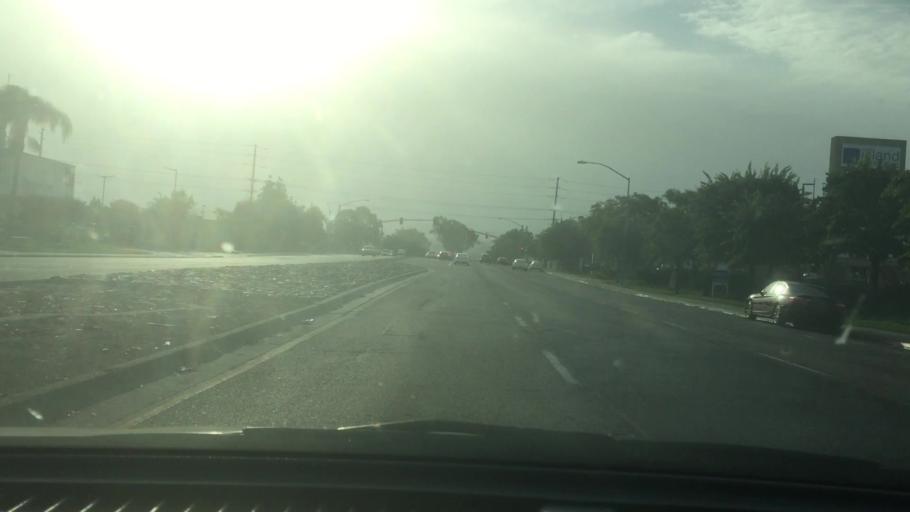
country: US
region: California
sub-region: San Diego County
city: San Diego
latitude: 32.8314
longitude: -117.1330
